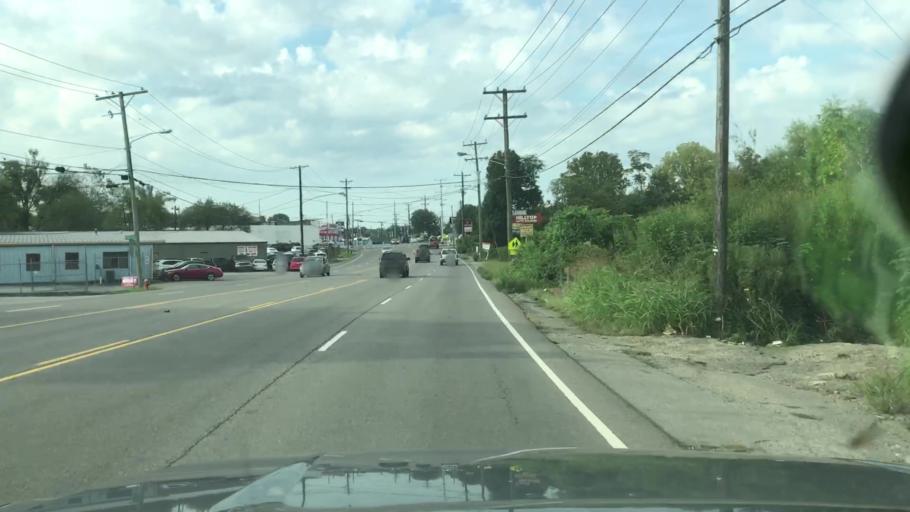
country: US
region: Tennessee
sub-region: Davidson County
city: Nashville
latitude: 36.2098
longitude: -86.7662
